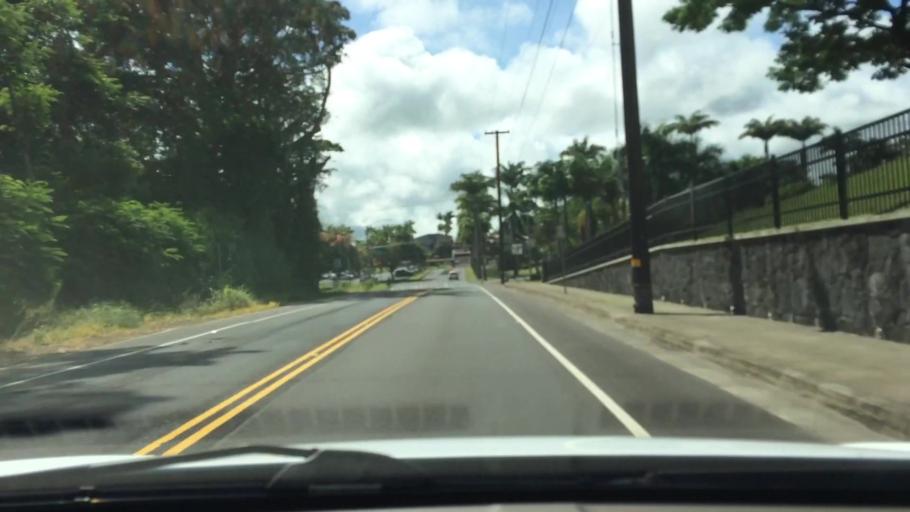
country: US
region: Hawaii
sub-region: Hawaii County
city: Hilo
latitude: 19.7019
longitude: -155.0779
